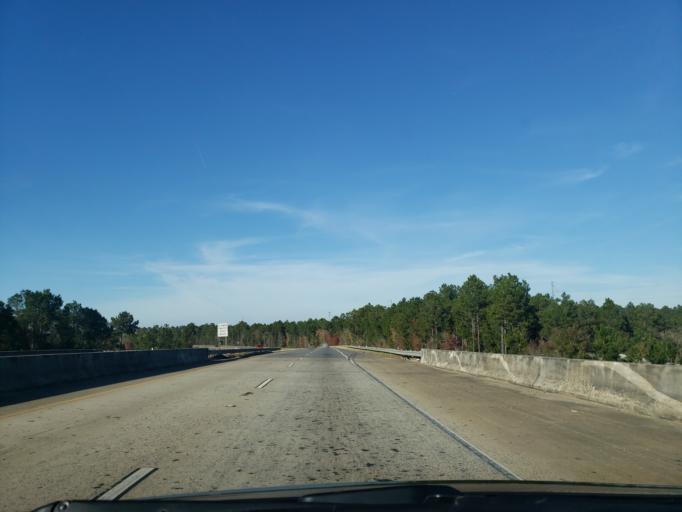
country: US
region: Georgia
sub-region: Ware County
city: Deenwood
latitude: 31.2349
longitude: -82.4268
